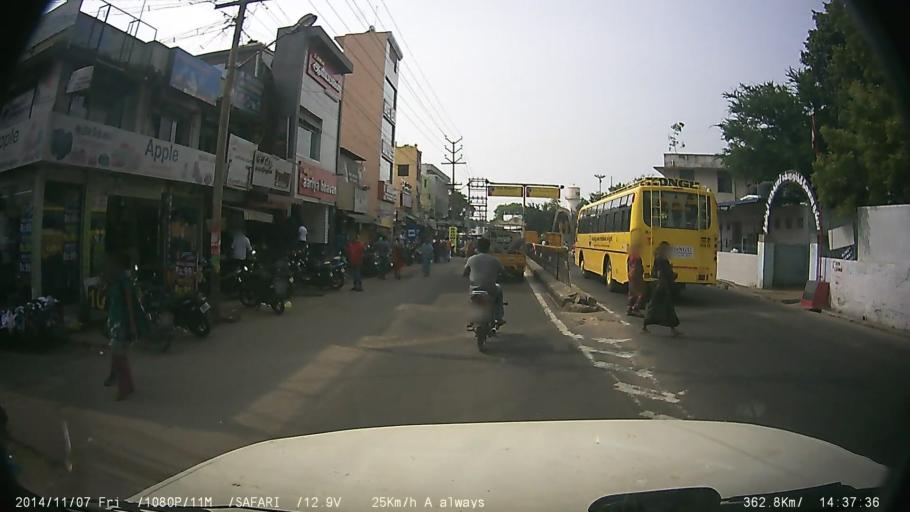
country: IN
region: Tamil Nadu
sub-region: Tiruppur
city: Tiruppur
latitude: 11.1071
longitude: 77.3406
